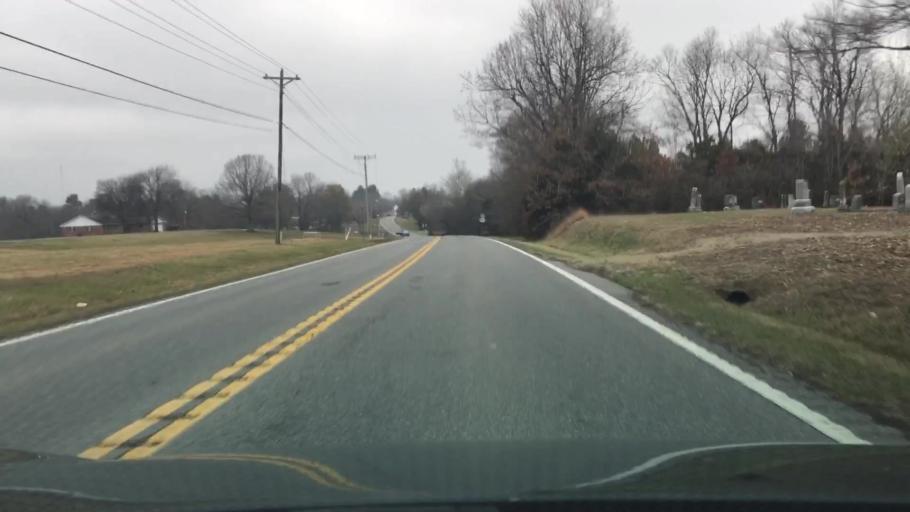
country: US
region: Kentucky
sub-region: Marshall County
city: Calvert City
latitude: 36.9553
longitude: -88.3718
